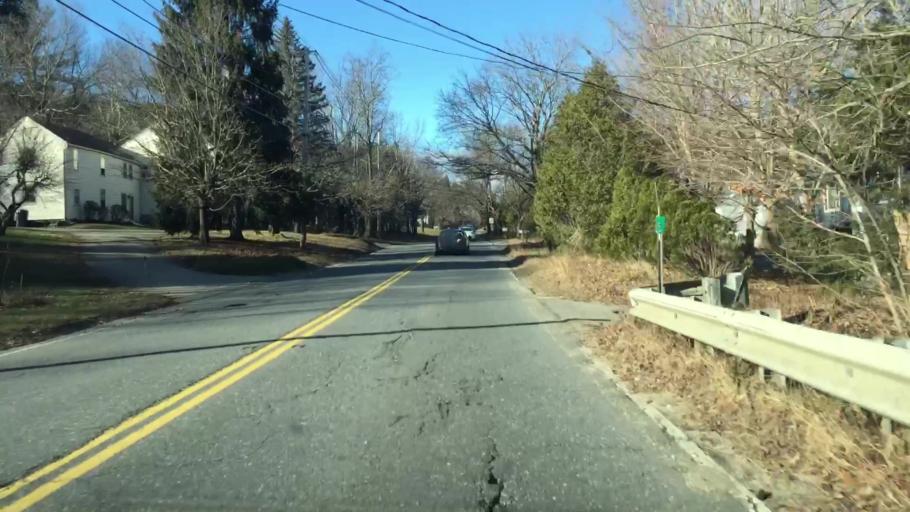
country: US
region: Massachusetts
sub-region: Worcester County
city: Sterling
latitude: 42.4162
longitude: -71.8029
